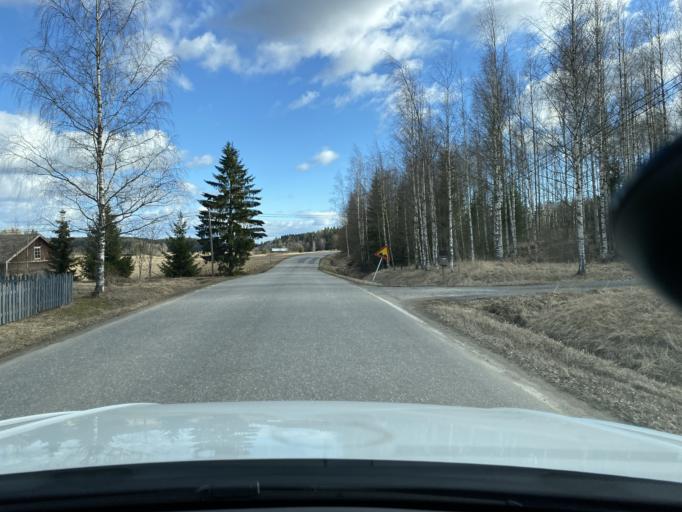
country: FI
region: Pirkanmaa
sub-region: Lounais-Pirkanmaa
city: Punkalaidun
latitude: 61.0893
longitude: 23.1506
